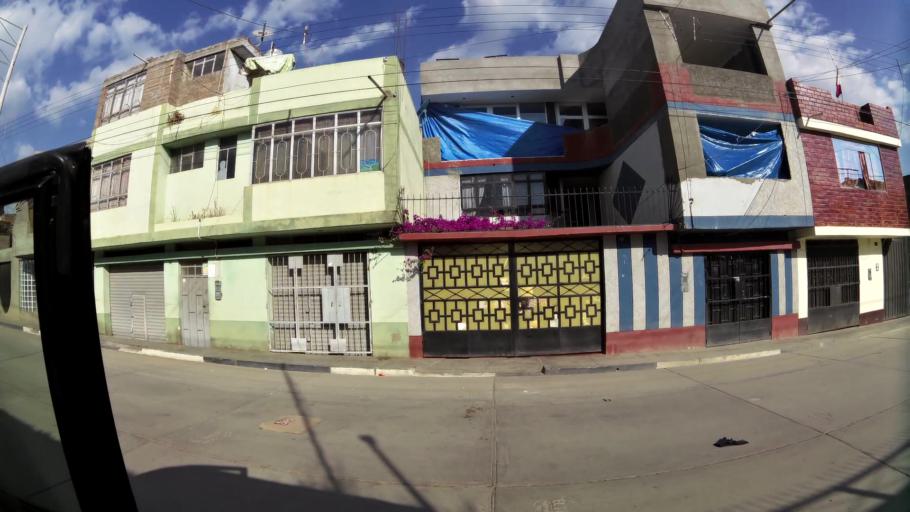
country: PE
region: Junin
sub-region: Provincia de Huancayo
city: El Tambo
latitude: -12.0573
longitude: -75.2273
